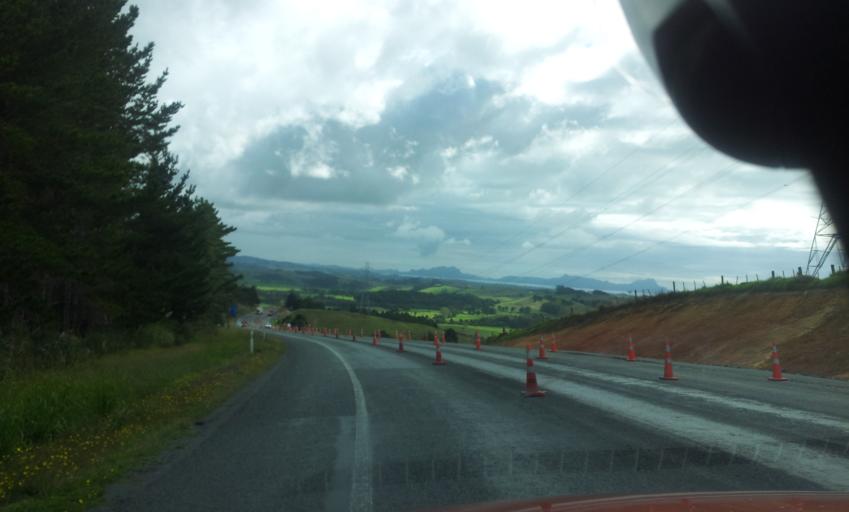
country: NZ
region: Northland
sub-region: Whangarei
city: Ruakaka
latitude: -36.0463
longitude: 174.4174
